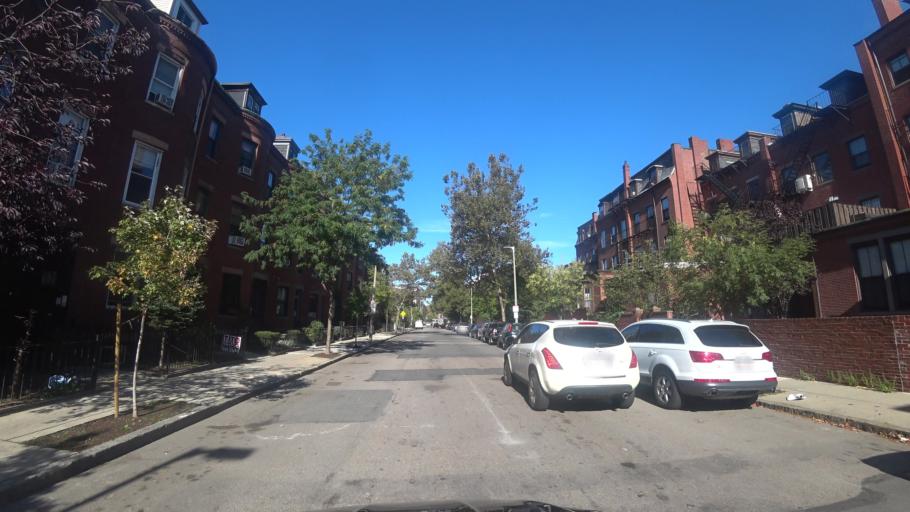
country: US
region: Massachusetts
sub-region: Suffolk County
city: Boston
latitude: 42.3375
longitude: -71.0796
